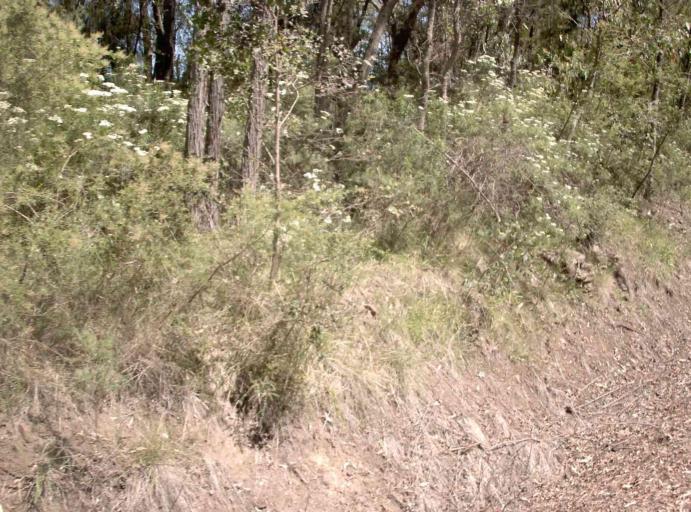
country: AU
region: Victoria
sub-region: East Gippsland
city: Lakes Entrance
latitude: -37.3546
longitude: 148.2286
